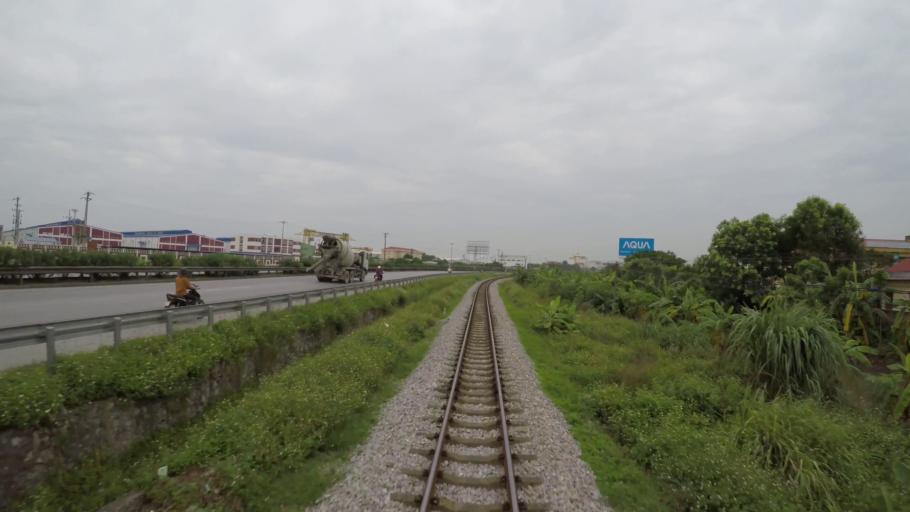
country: VN
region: Hai Duong
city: Nam Sach
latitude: 20.9781
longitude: 106.4142
